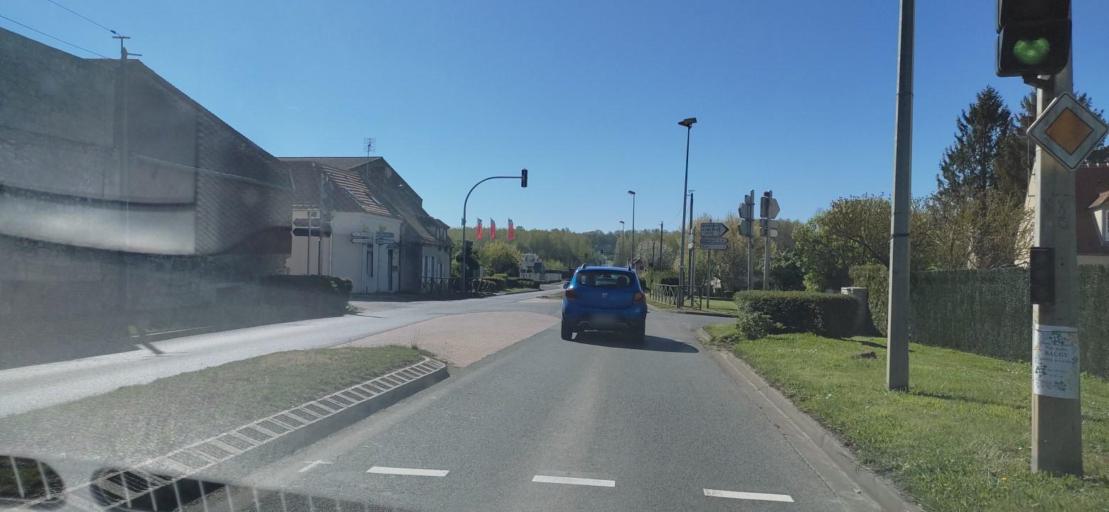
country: FR
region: Picardie
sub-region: Departement de l'Oise
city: Villers-sur-Coudun
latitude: 49.4708
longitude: 2.7562
